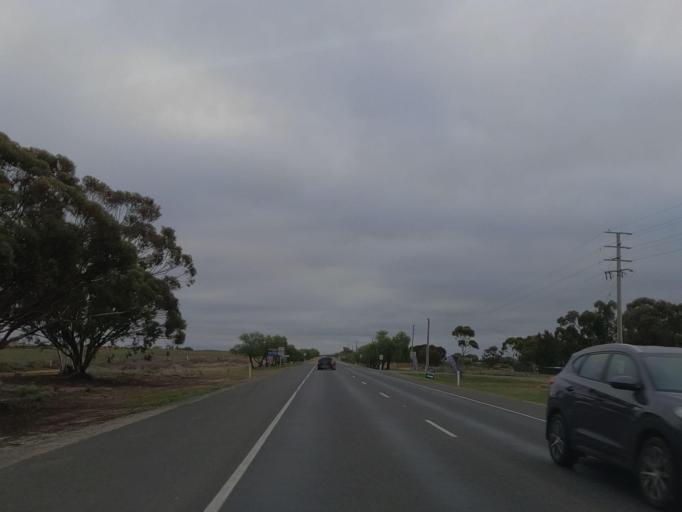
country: AU
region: Victoria
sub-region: Swan Hill
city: Swan Hill
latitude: -35.4505
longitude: 143.6241
